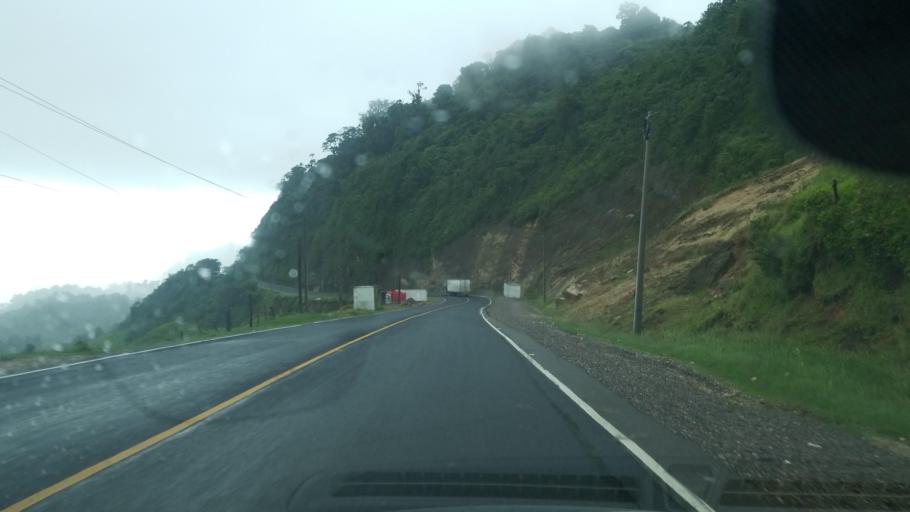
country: HN
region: Ocotepeque
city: La Labor
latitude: 14.4650
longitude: -89.0733
